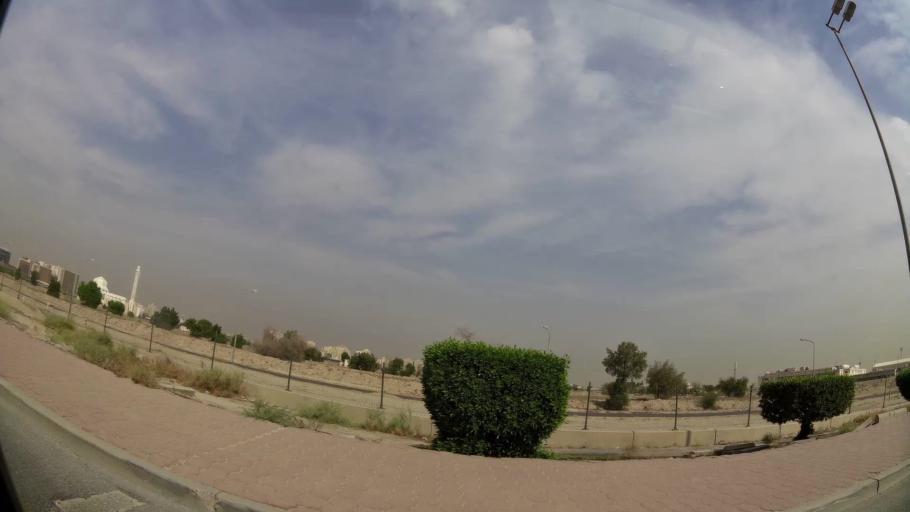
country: KW
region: Al Farwaniyah
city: Janub as Surrah
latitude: 29.2663
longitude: 47.9752
